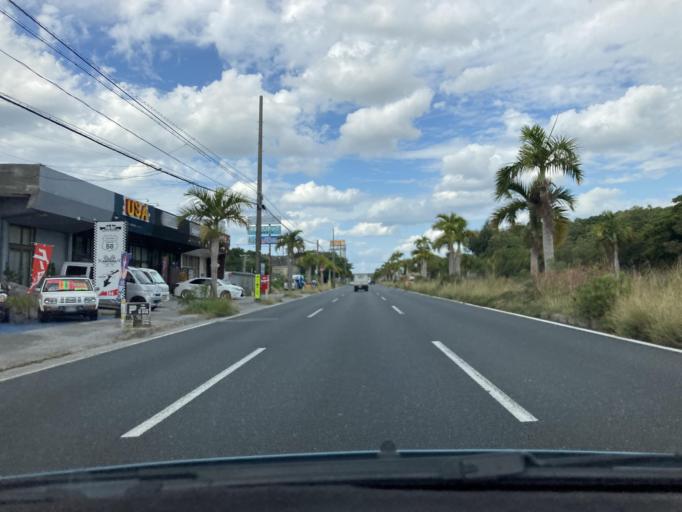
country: JP
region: Okinawa
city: Chatan
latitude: 26.3330
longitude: 127.7515
